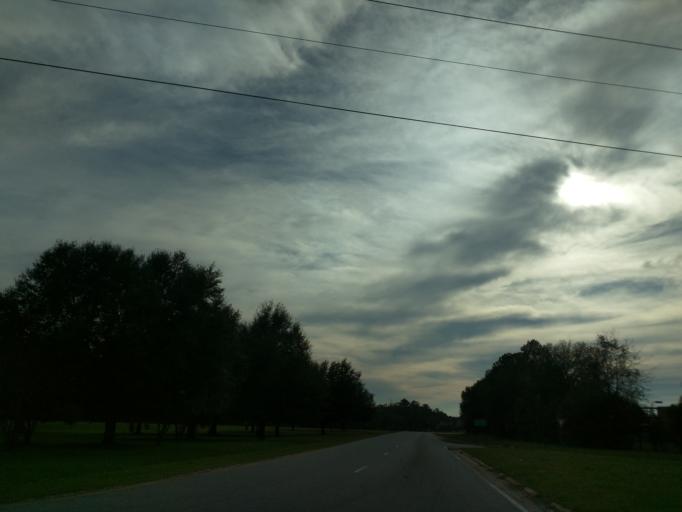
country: US
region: Georgia
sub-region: Decatur County
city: Bainbridge
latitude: 30.9035
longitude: -84.5432
